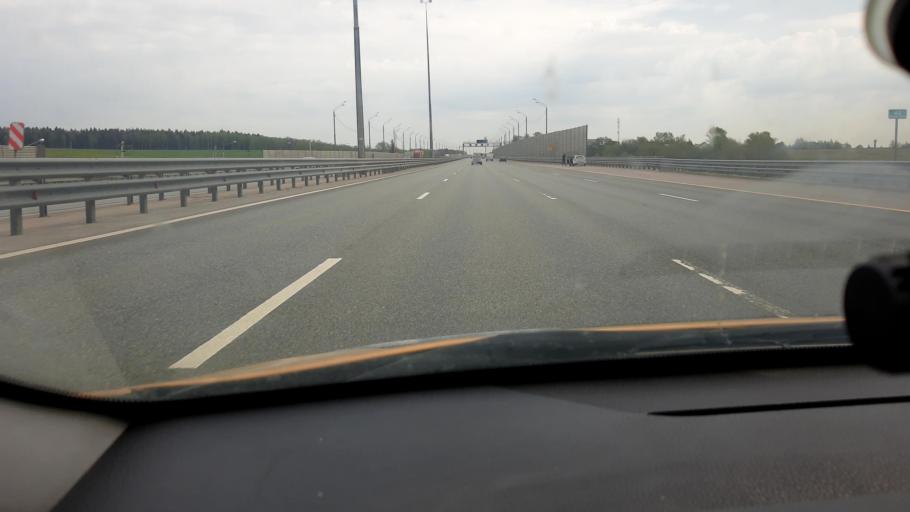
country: RU
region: Moskovskaya
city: Rozhdestveno
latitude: 55.8200
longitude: 36.9924
